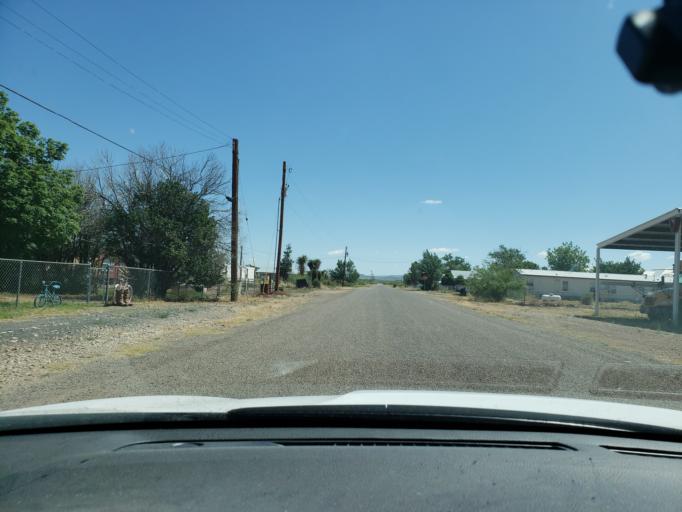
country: US
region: Texas
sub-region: Presidio County
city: Marfa
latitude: 30.5895
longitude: -104.4942
